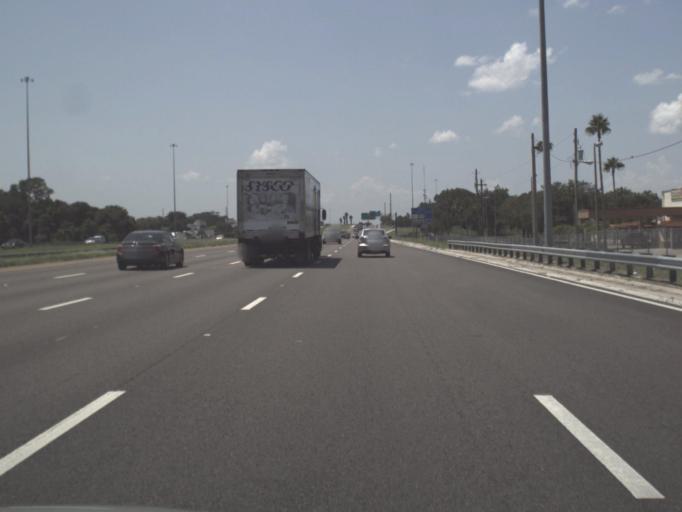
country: US
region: Florida
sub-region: Hillsborough County
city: East Lake-Orient Park
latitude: 27.9871
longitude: -82.3774
